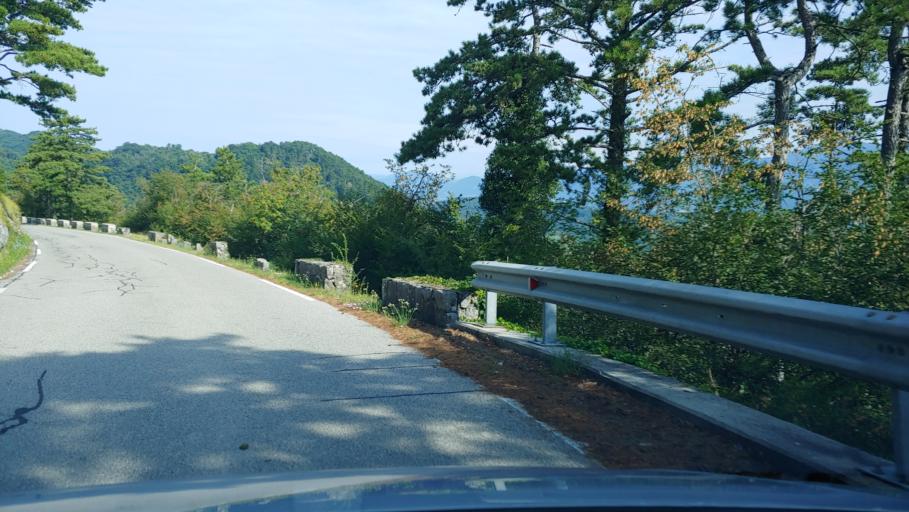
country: SI
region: Komen
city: Komen
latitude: 45.8487
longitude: 13.7880
